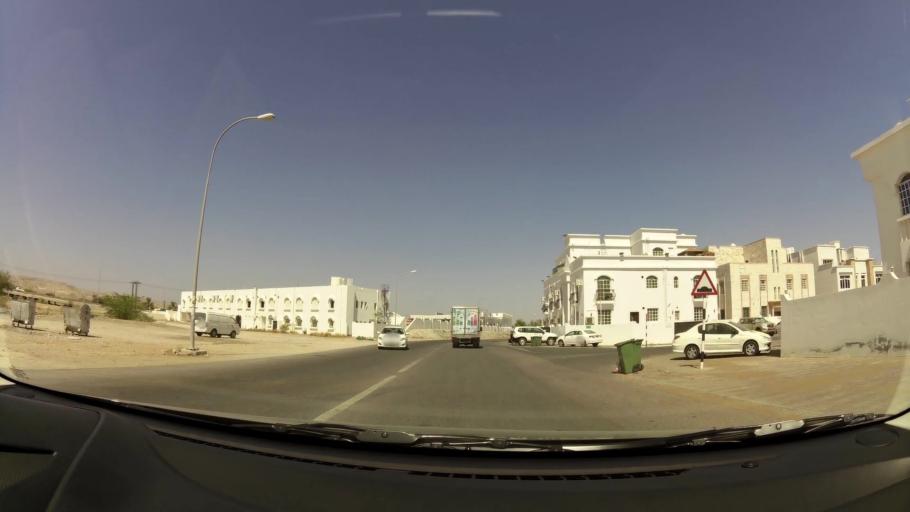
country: OM
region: Muhafazat Masqat
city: As Sib al Jadidah
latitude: 23.5912
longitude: 58.2446
